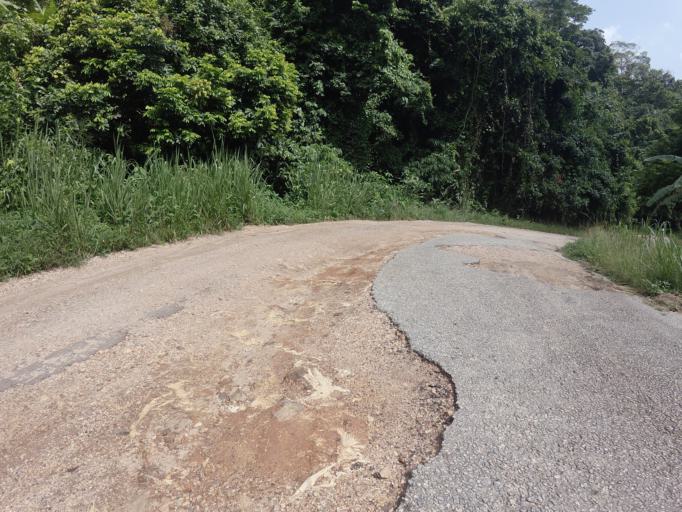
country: GH
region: Volta
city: Kpandu
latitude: 6.8336
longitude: 0.4265
